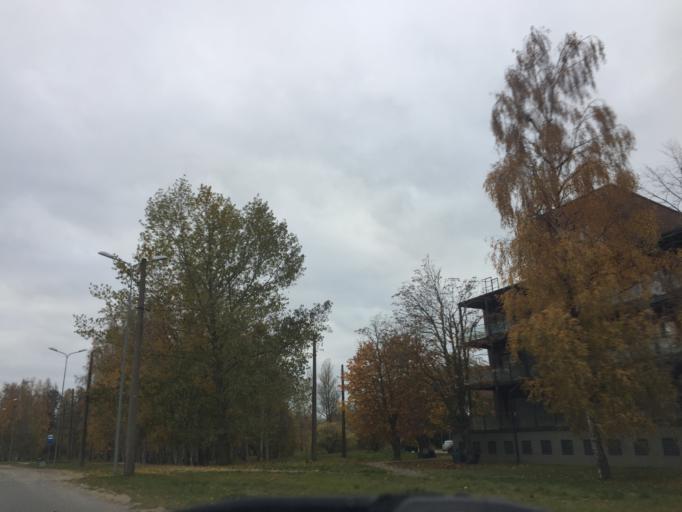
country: LV
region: Liepaja
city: Liepaja
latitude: 56.4852
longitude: 21.0059
